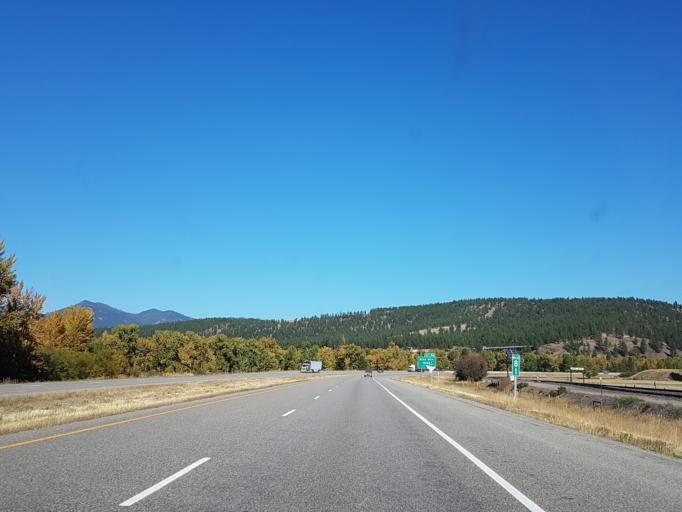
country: US
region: Montana
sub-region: Missoula County
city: Frenchtown
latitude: 47.0212
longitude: -114.3956
